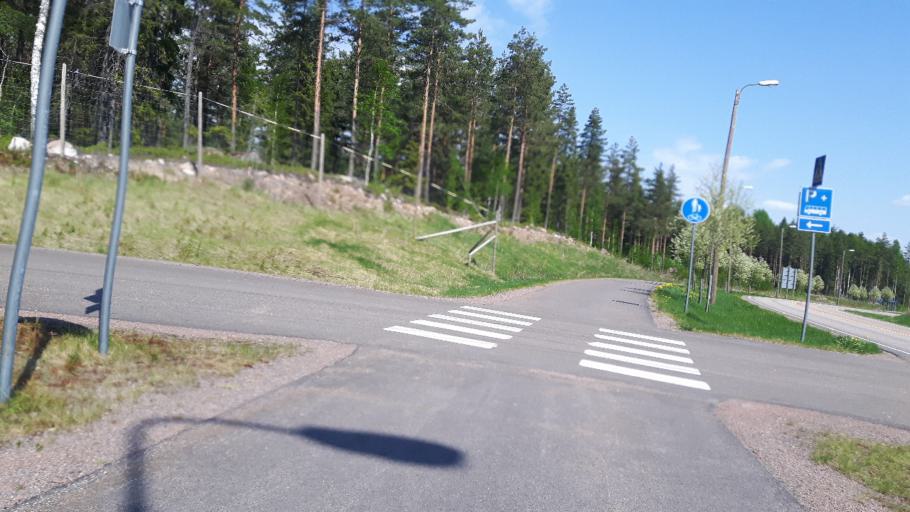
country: FI
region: Uusimaa
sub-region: Loviisa
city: Ruotsinpyhtaeae
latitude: 60.4939
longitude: 26.4200
